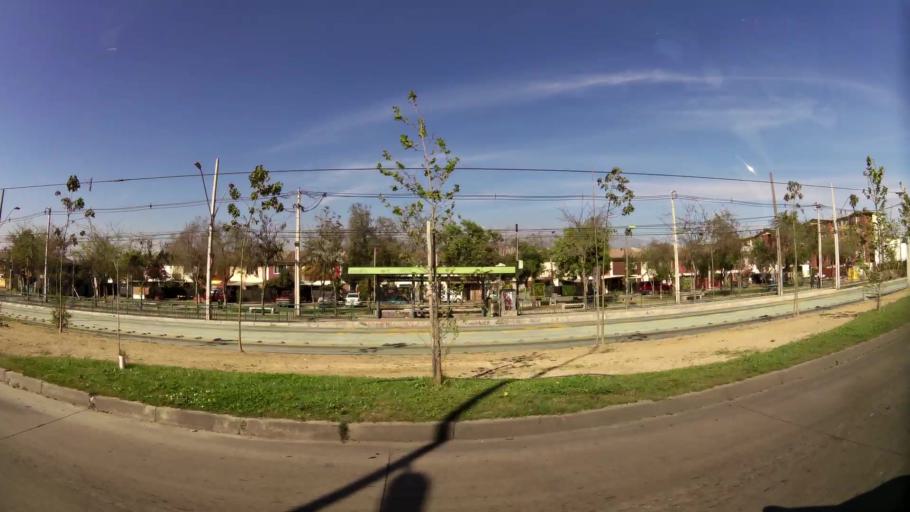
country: CL
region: Santiago Metropolitan
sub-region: Provincia de Santiago
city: Santiago
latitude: -33.4880
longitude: -70.6298
